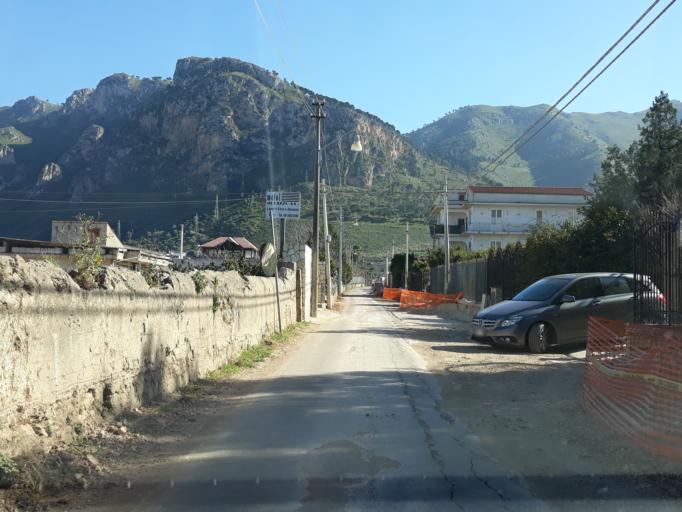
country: IT
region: Sicily
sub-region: Palermo
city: Villa Ciambra
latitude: 38.0810
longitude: 13.3465
